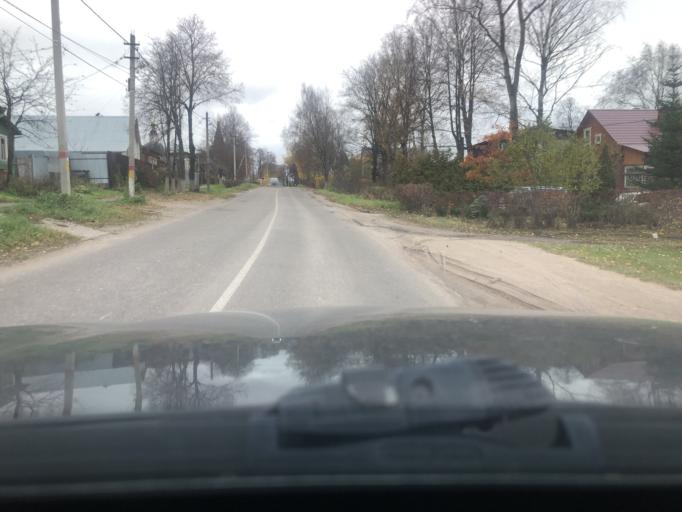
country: RU
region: Moskovskaya
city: Sergiyev Posad
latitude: 56.3023
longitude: 38.1241
